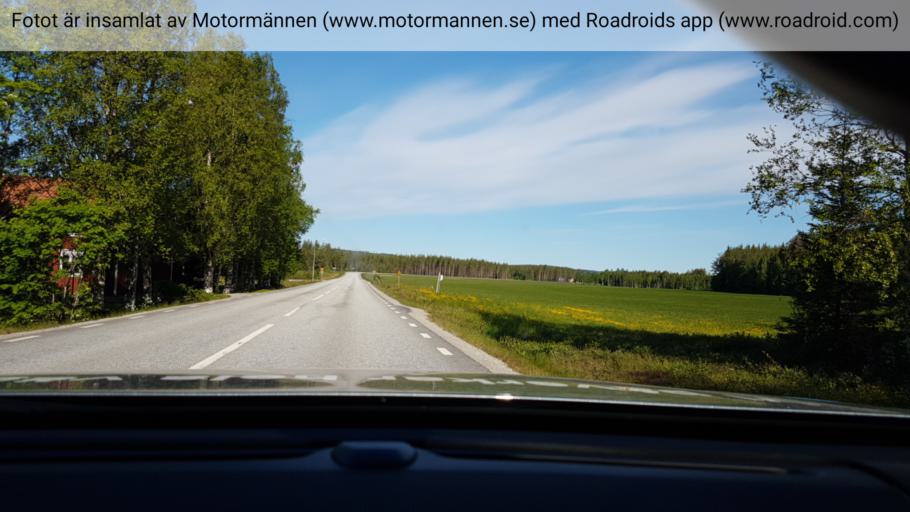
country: SE
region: Vaesterbotten
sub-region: Vindelns Kommun
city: Vindeln
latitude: 64.1128
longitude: 19.5802
